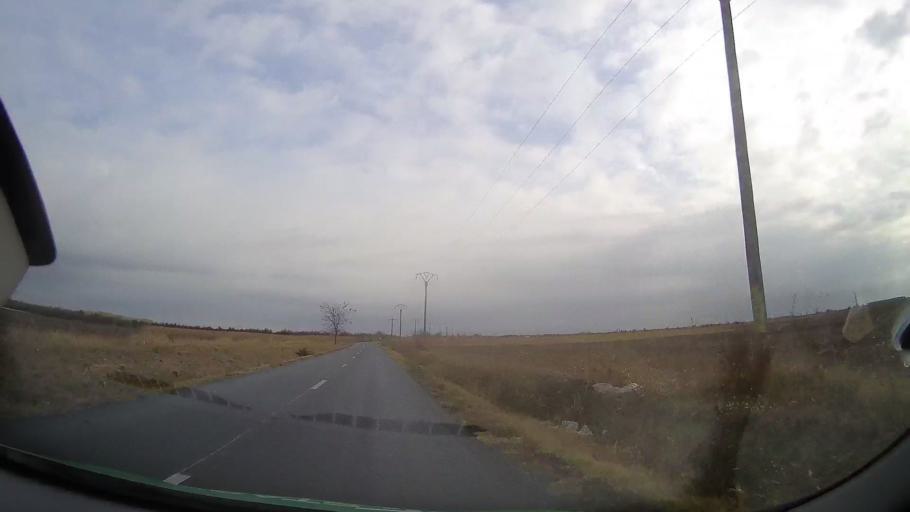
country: RO
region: Ialomita
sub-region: Comuna Maia
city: Maia
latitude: 44.7547
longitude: 26.3825
